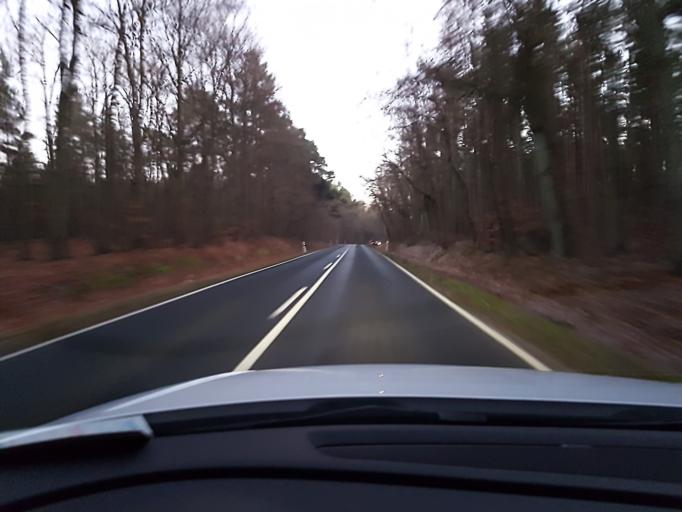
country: DE
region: Mecklenburg-Vorpommern
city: Gingst
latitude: 54.5072
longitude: 13.2756
